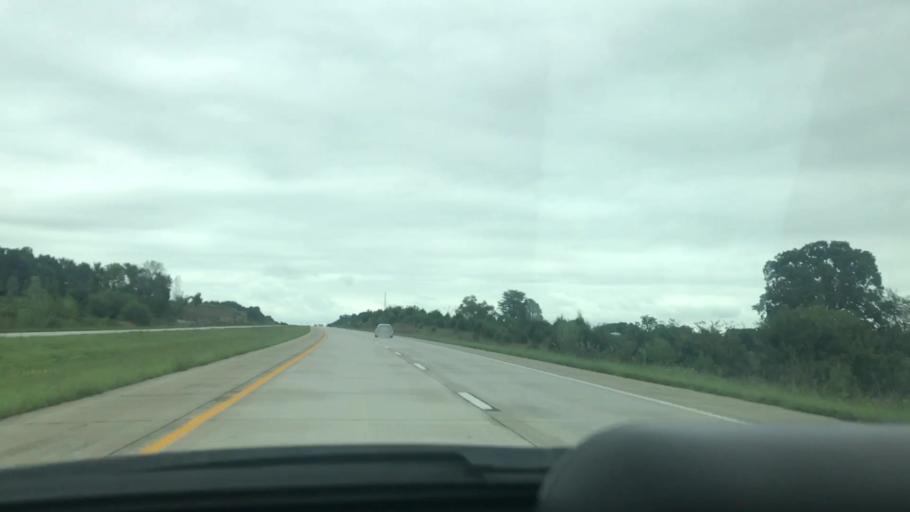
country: US
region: Missouri
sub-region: Dallas County
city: Buffalo
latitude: 37.5322
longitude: -93.1371
